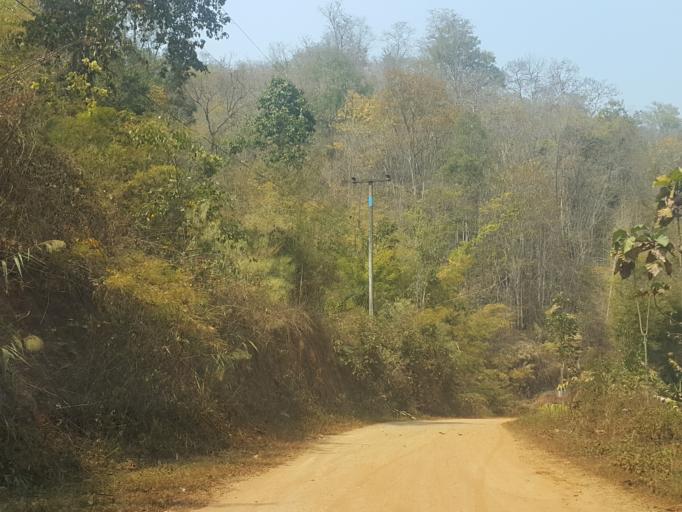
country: TH
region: Chiang Mai
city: Hang Dong
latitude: 18.7459
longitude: 98.8263
